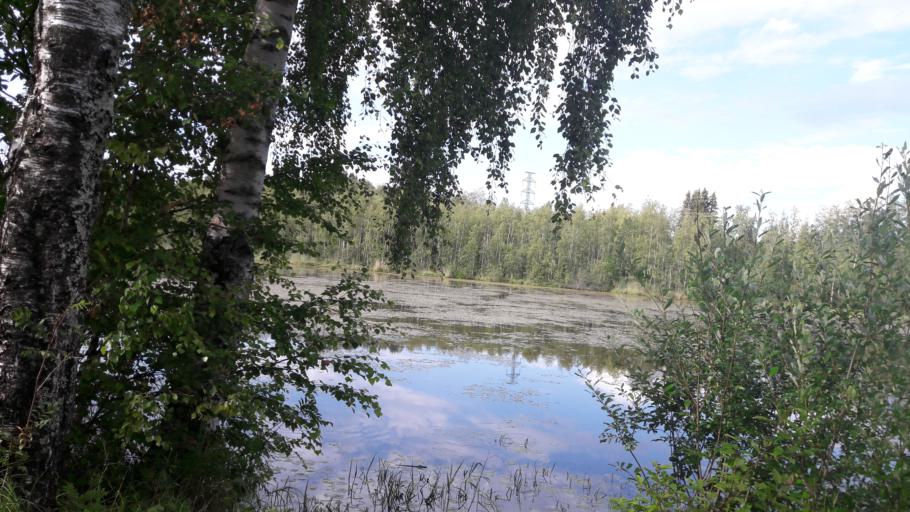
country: FI
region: North Karelia
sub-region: Joensuu
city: Joensuu
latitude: 62.5990
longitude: 29.7897
